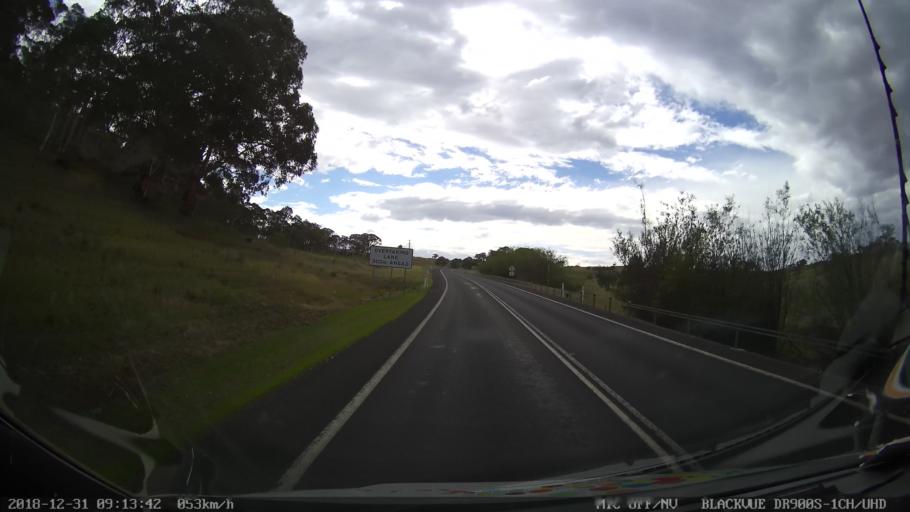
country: AU
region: New South Wales
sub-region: Snowy River
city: Jindabyne
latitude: -36.3699
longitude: 148.5918
